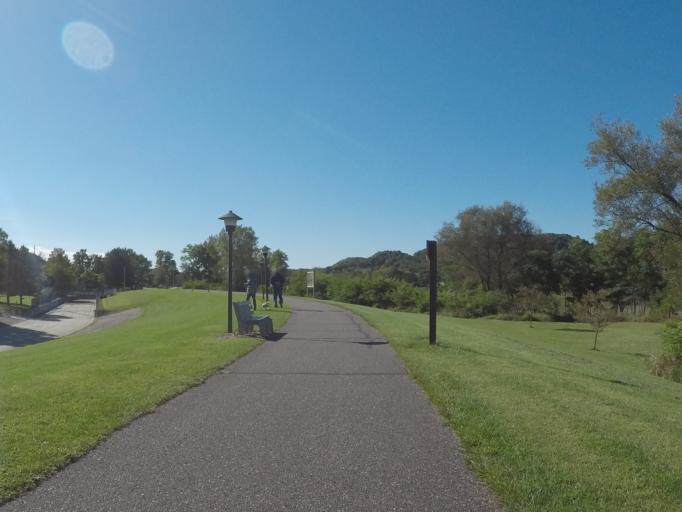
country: US
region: Wisconsin
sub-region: Richland County
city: Richland Center
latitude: 43.3408
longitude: -90.3914
